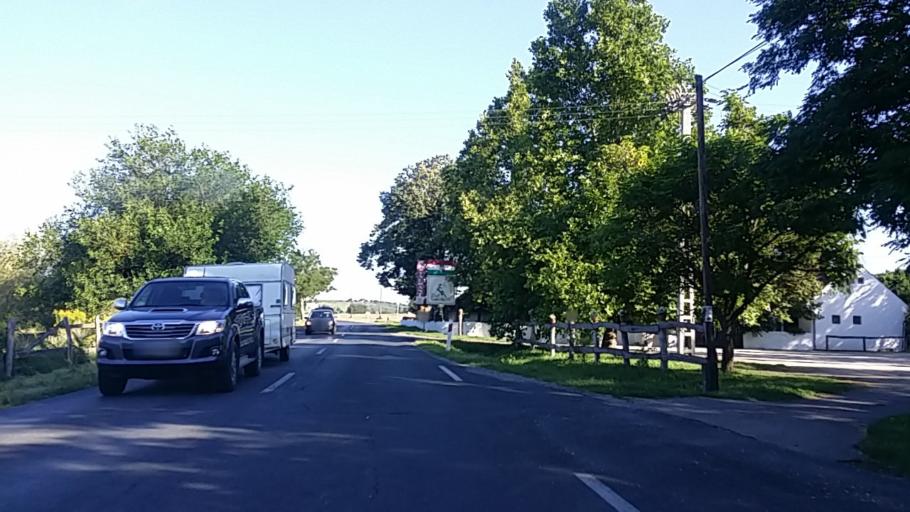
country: HU
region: Zala
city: Cserszegtomaj
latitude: 46.8278
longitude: 17.1985
